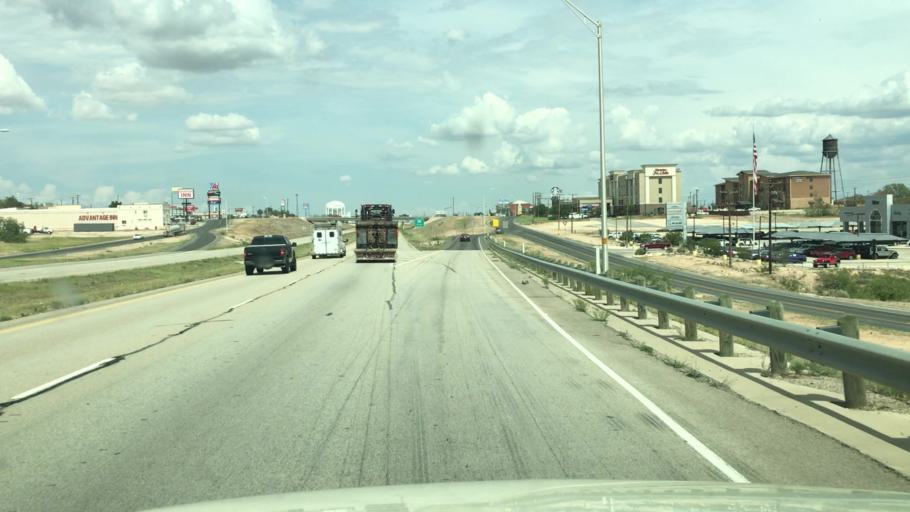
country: US
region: Texas
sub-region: Howard County
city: Big Spring
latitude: 32.2622
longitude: -101.4960
